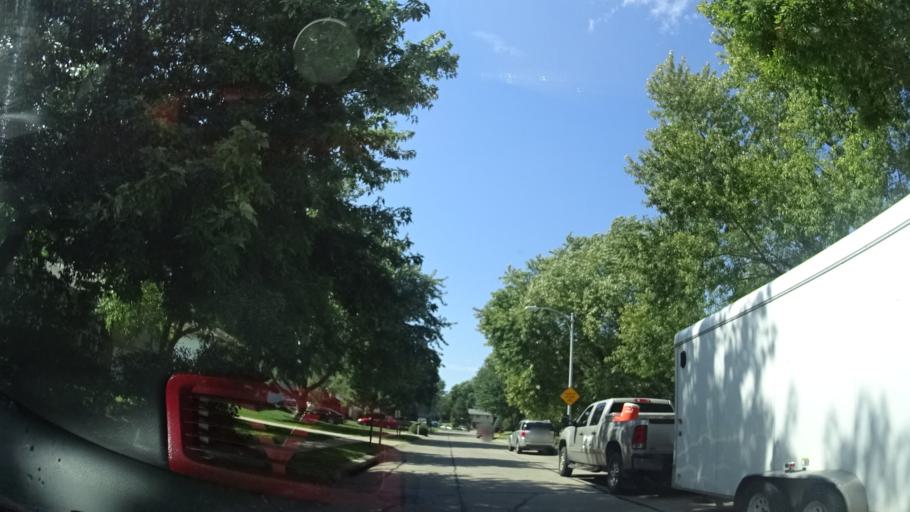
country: US
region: Nebraska
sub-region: Sarpy County
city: Offutt Air Force Base
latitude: 41.1315
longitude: -95.9537
